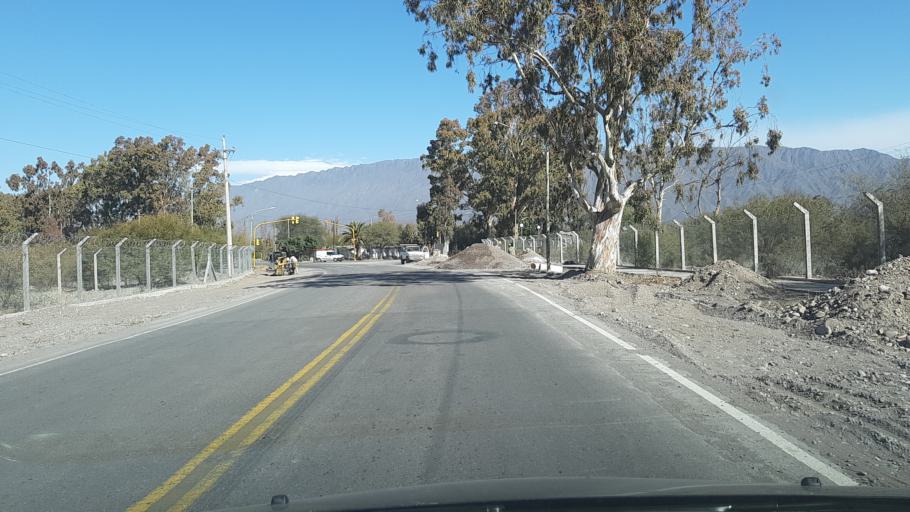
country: AR
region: San Juan
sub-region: Departamento de Zonda
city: Zonda
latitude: -31.5460
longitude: -68.7188
